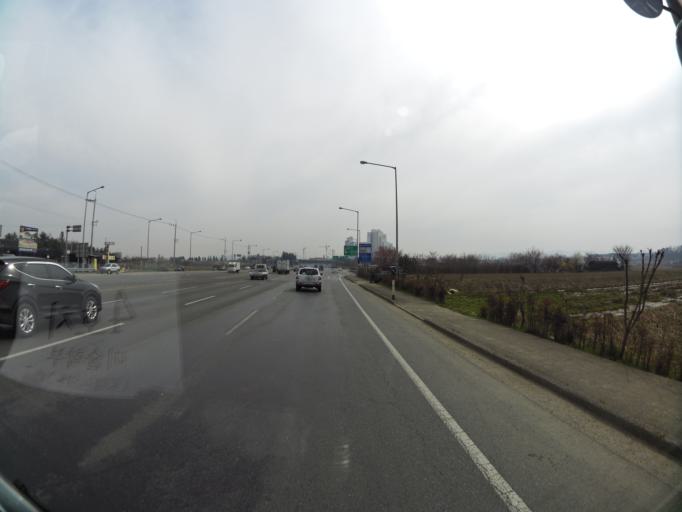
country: KR
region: Gyeongsangbuk-do
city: Hayang
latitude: 35.8737
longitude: 128.7920
